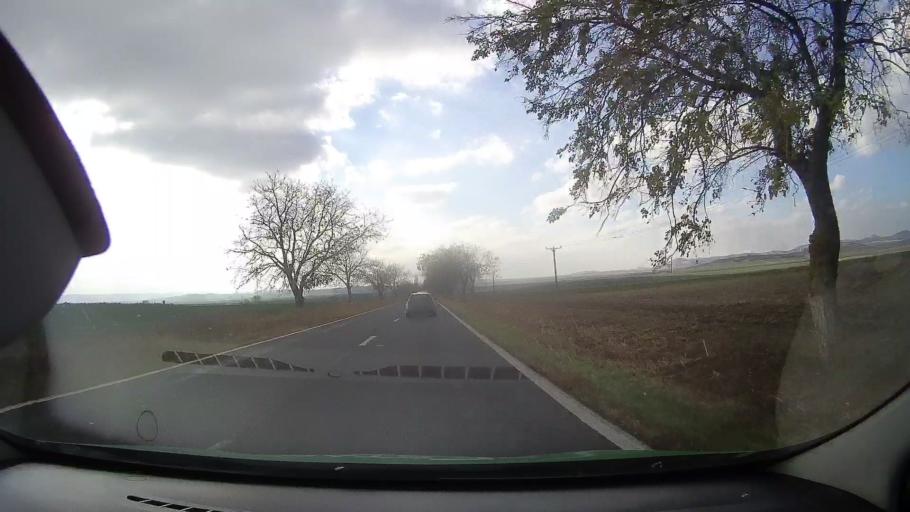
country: RO
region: Tulcea
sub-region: Comuna Frecatei
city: Frecatei
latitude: 45.0691
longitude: 28.6542
